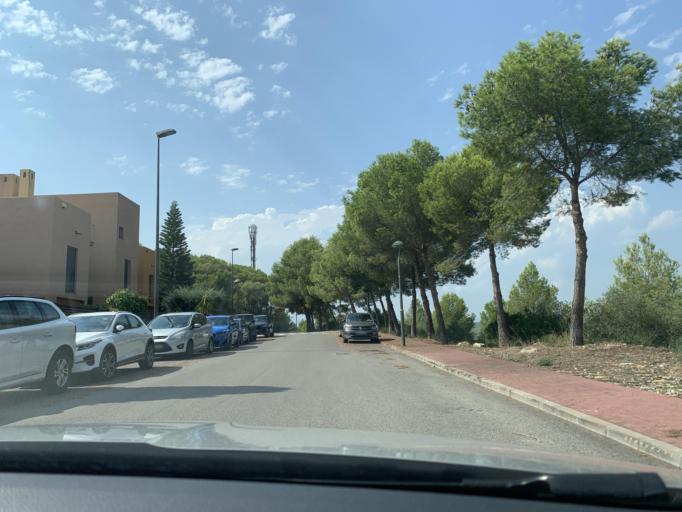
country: ES
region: Catalonia
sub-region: Provincia de Tarragona
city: Altafulla
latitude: 41.1335
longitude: 1.3558
